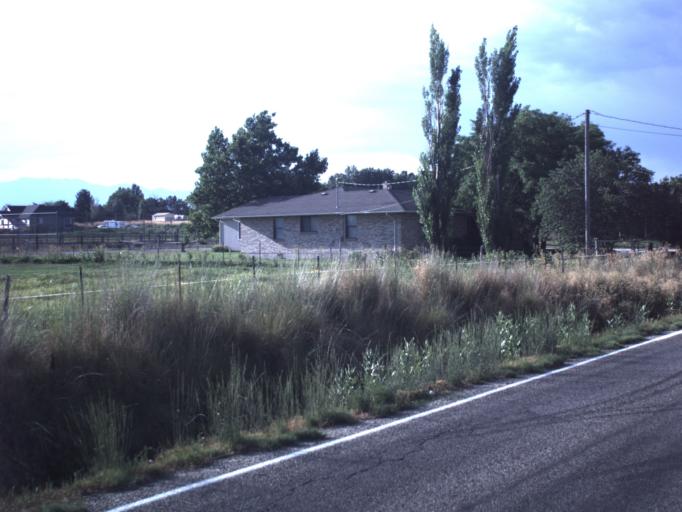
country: US
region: Utah
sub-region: Weber County
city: West Haven
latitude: 41.2181
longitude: -112.0929
